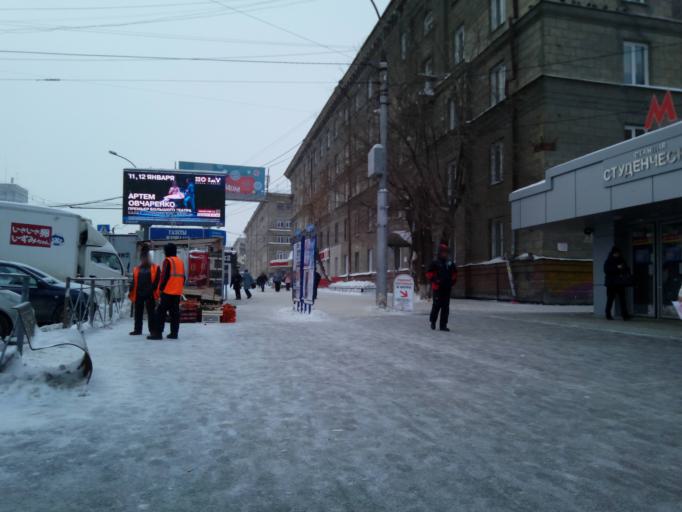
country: RU
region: Novosibirsk
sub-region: Novosibirskiy Rayon
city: Novosibirsk
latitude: 54.9889
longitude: 82.9055
